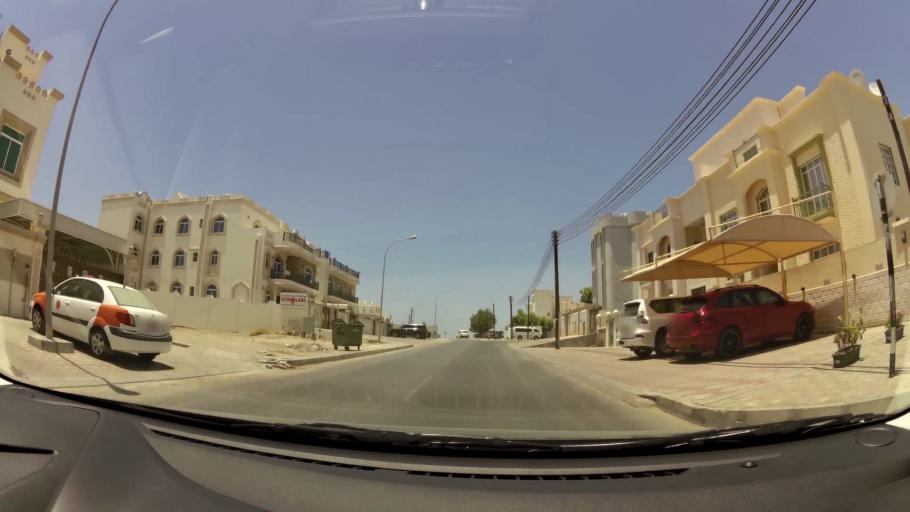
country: OM
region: Muhafazat Masqat
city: Bawshar
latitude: 23.6016
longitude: 58.3855
